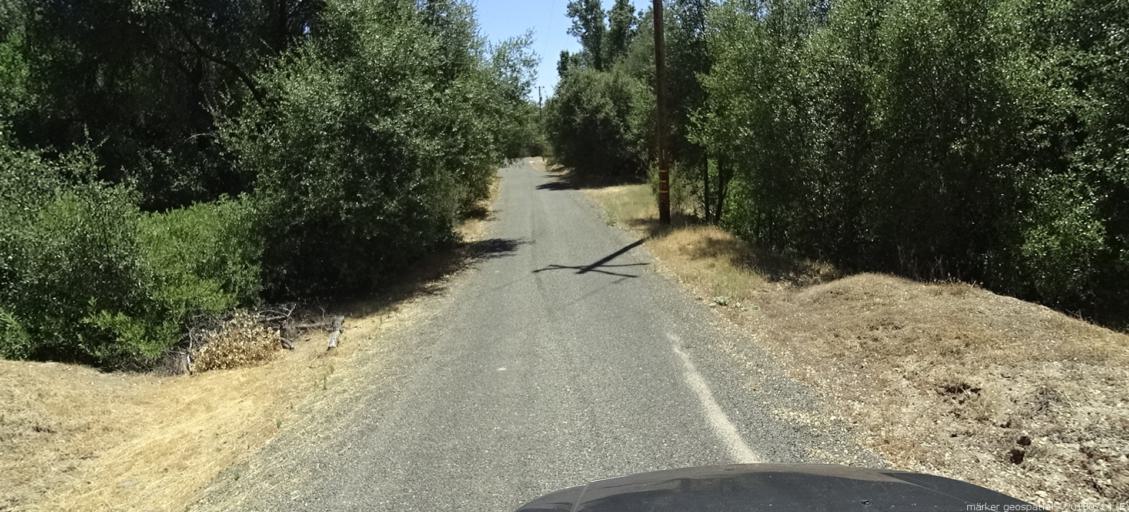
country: US
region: California
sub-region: Madera County
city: Ahwahnee
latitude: 37.3774
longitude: -119.7419
